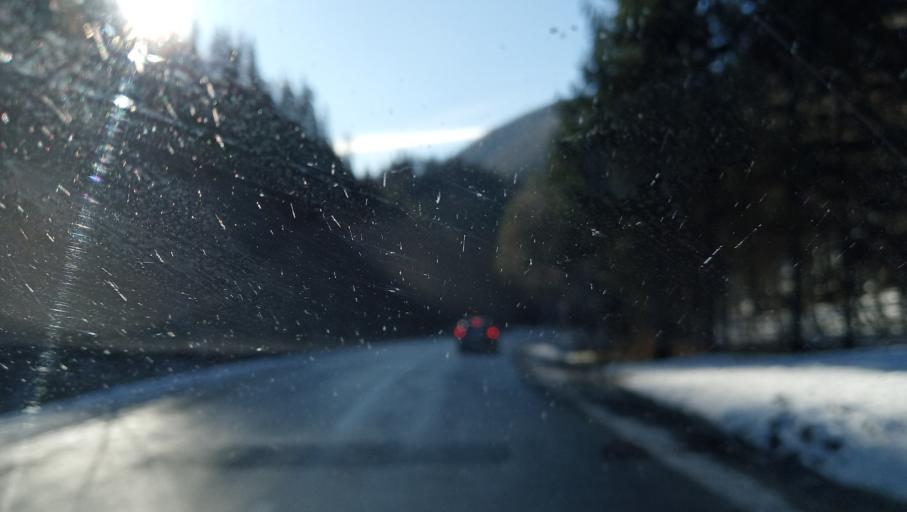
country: RO
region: Brasov
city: Crivina
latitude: 45.4795
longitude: 25.9203
